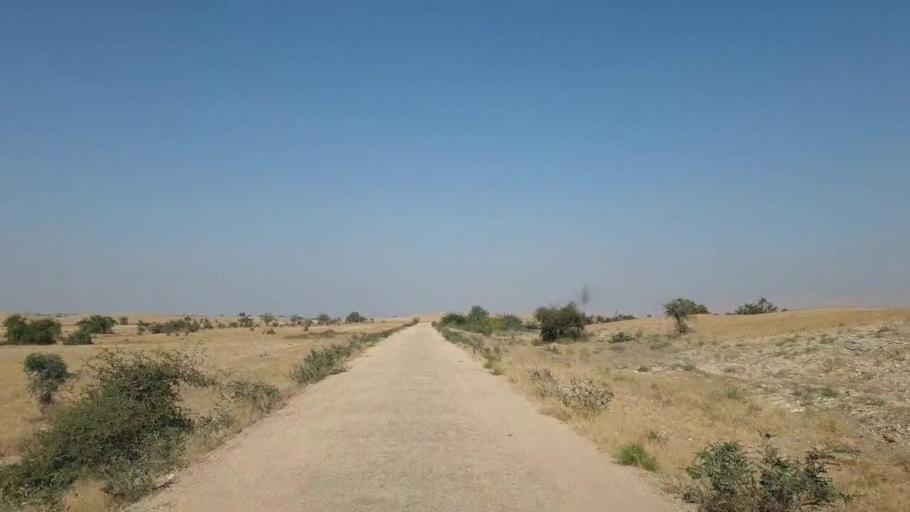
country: PK
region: Sindh
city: Jamshoro
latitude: 25.4916
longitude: 67.8393
